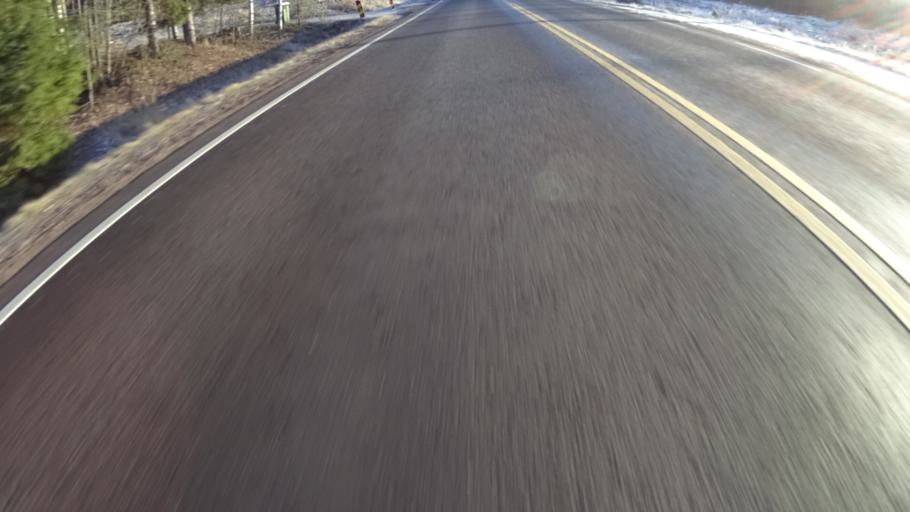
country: FI
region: Uusimaa
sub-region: Helsinki
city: Vihti
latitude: 60.5134
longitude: 24.4255
